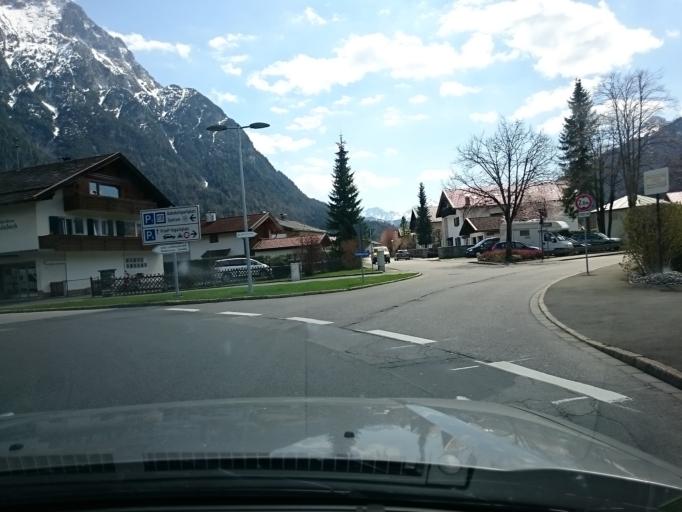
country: DE
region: Bavaria
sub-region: Upper Bavaria
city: Mittenwald
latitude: 47.4471
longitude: 11.2675
